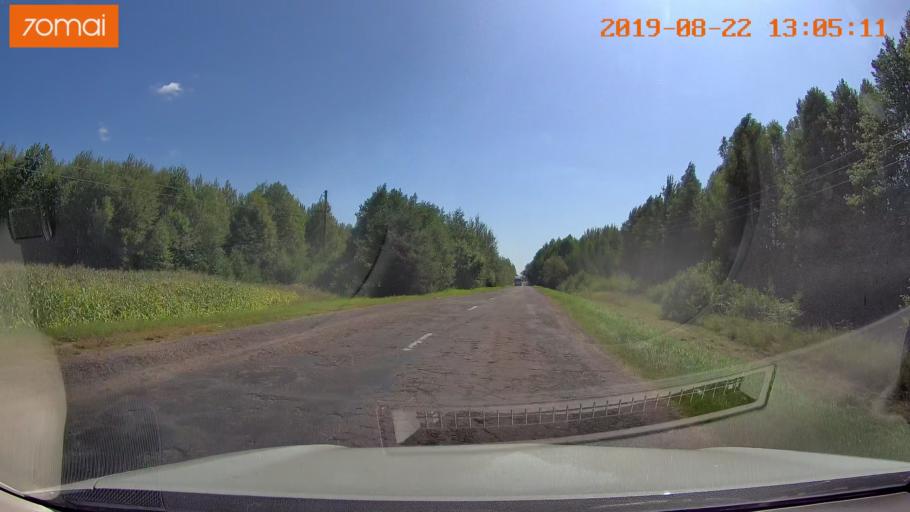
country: BY
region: Minsk
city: Prawdzinski
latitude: 53.3620
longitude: 27.8323
